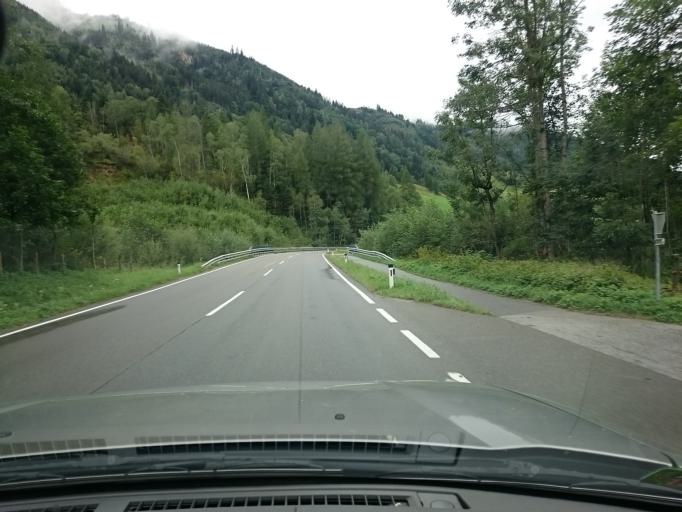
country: AT
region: Salzburg
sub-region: Politischer Bezirk Zell am See
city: Bruck an der Grossglocknerstrasse
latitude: 47.2507
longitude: 12.8260
